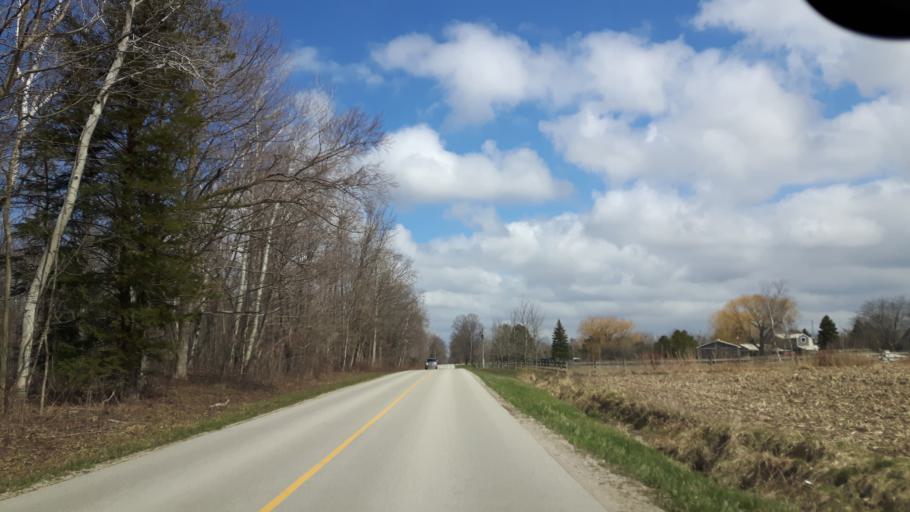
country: CA
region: Ontario
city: Goderich
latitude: 43.6199
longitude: -81.6846
